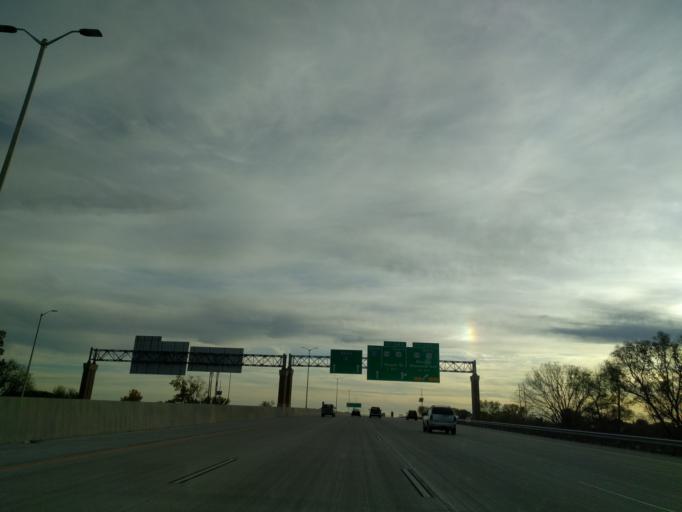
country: US
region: Wisconsin
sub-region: Brown County
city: Howard
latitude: 44.5515
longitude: -88.0662
